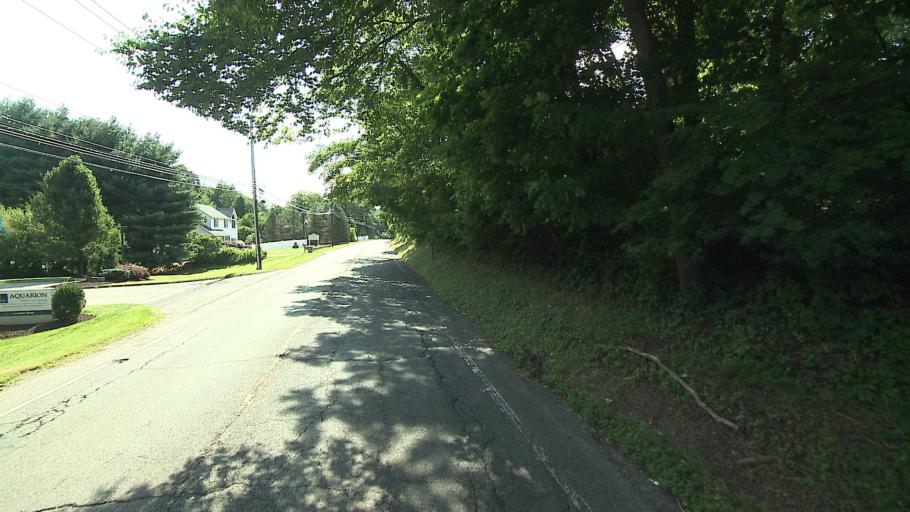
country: US
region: Connecticut
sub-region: Litchfield County
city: New Milford
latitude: 41.5805
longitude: -73.4265
